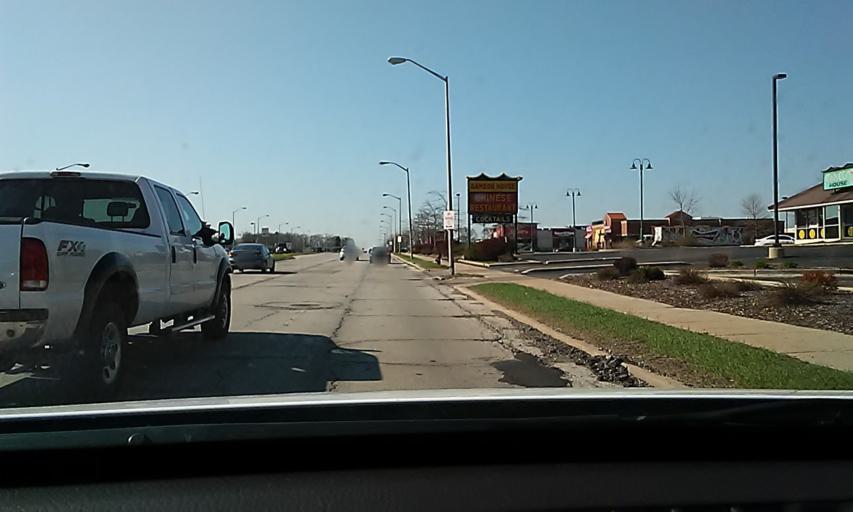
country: US
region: Wisconsin
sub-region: Milwaukee County
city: Greenfield
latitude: 42.9926
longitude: -88.0472
